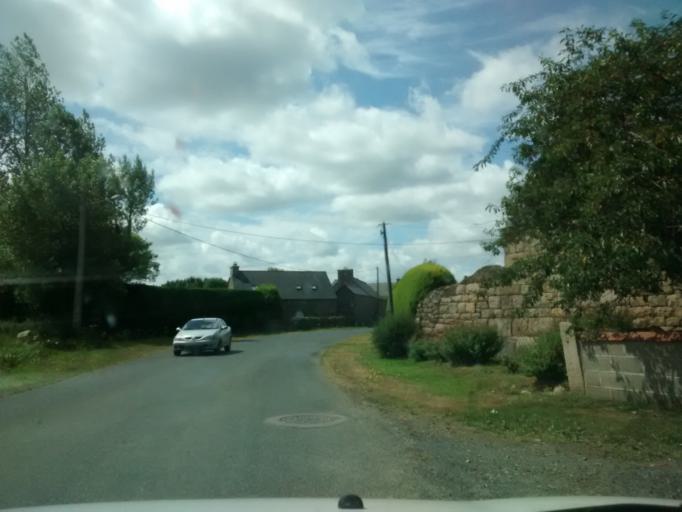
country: FR
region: Brittany
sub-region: Departement des Cotes-d'Armor
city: Penvenan
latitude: 48.8220
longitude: -3.2829
